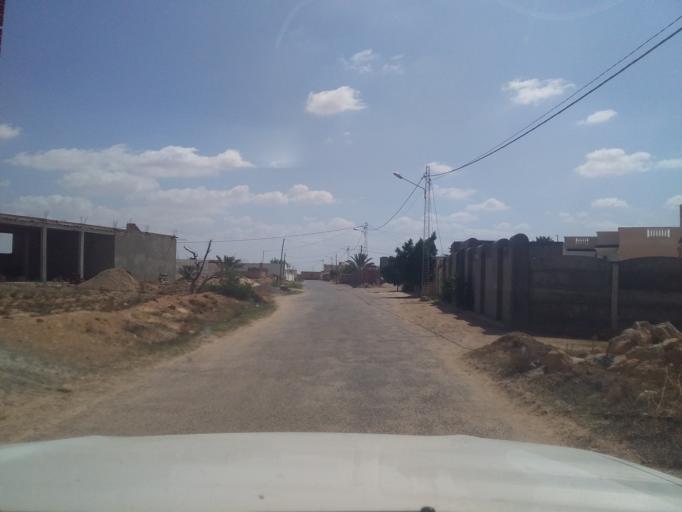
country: TN
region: Madanin
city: Medenine
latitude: 33.6130
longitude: 10.2999
